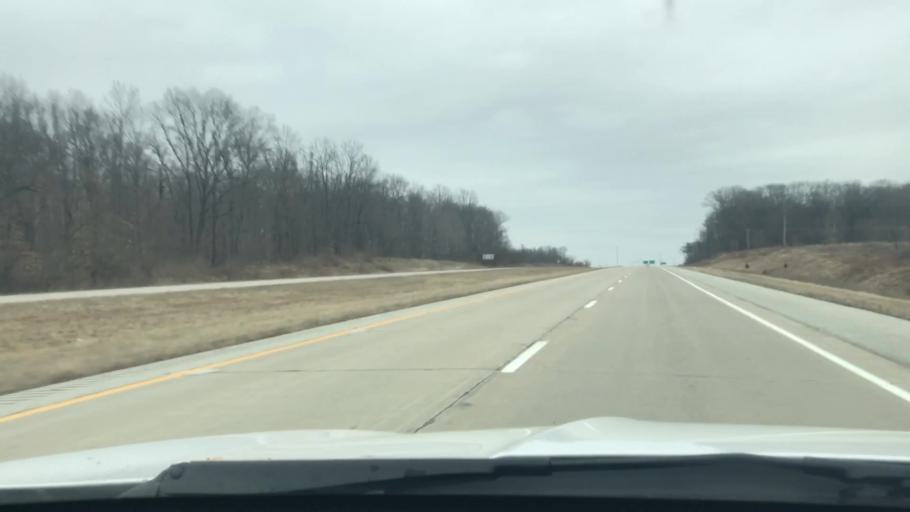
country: US
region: Indiana
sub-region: Miami County
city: Peru
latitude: 40.7705
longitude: -86.1458
